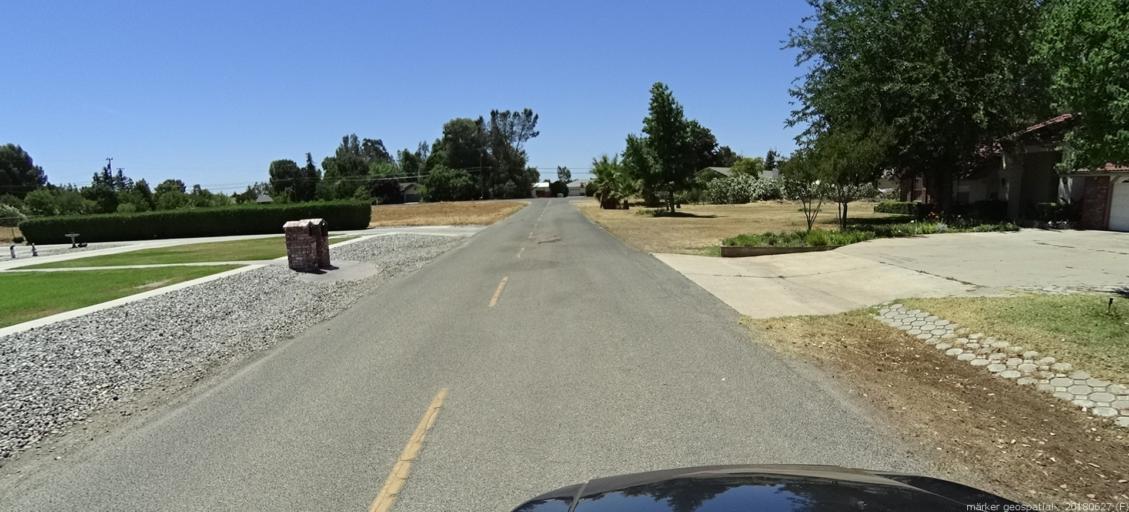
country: US
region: California
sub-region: Madera County
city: Bonadelle Ranchos-Madera Ranchos
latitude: 36.9296
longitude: -119.8709
